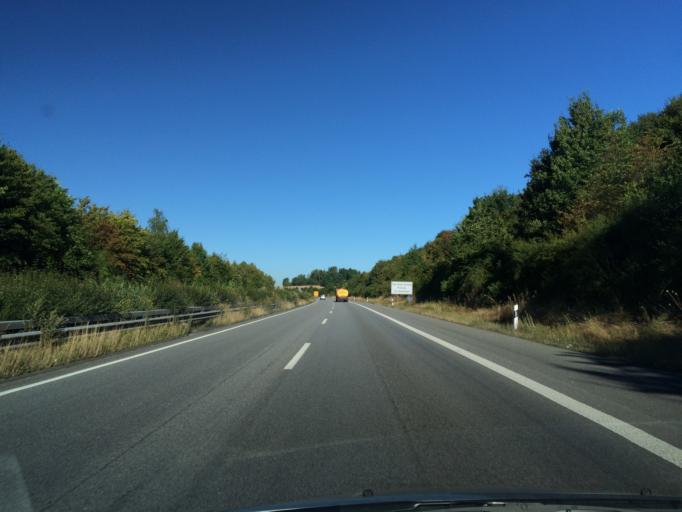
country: DE
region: Rheinland-Pfalz
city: Walshausen
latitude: 49.2174
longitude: 7.4914
